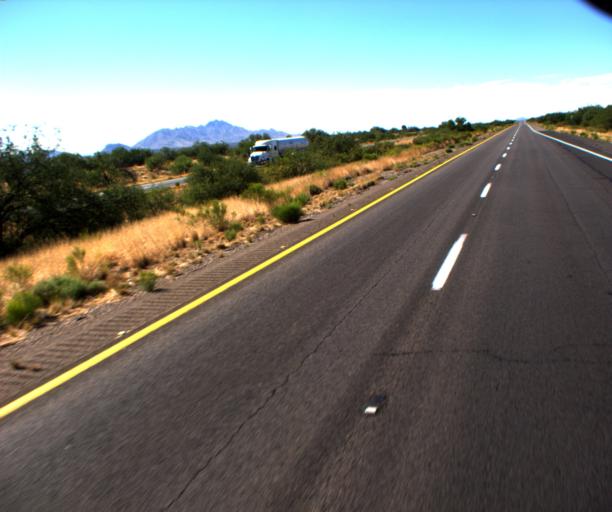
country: US
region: Arizona
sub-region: Santa Cruz County
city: Tubac
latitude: 31.6470
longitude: -111.0587
